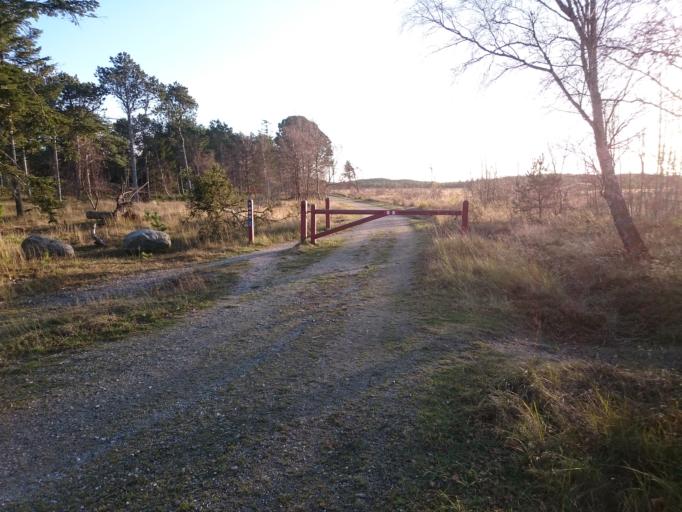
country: DK
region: North Denmark
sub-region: Frederikshavn Kommune
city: Skagen
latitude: 57.7138
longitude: 10.5442
